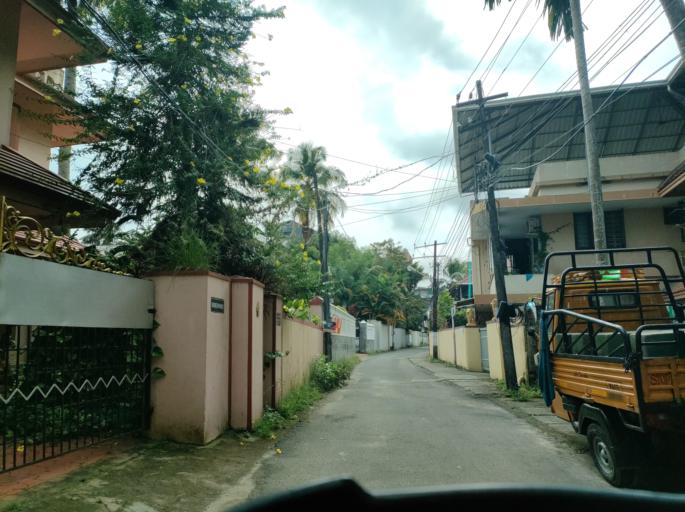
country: IN
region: Kerala
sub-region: Ernakulam
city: Elur
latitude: 9.9967
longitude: 76.3091
